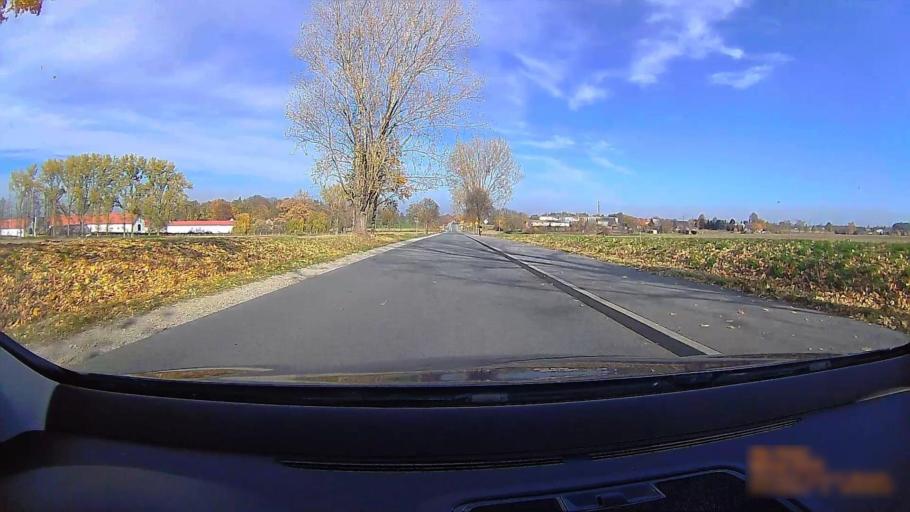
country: PL
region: Greater Poland Voivodeship
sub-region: Powiat kepinski
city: Kepno
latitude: 51.3419
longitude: 18.0227
